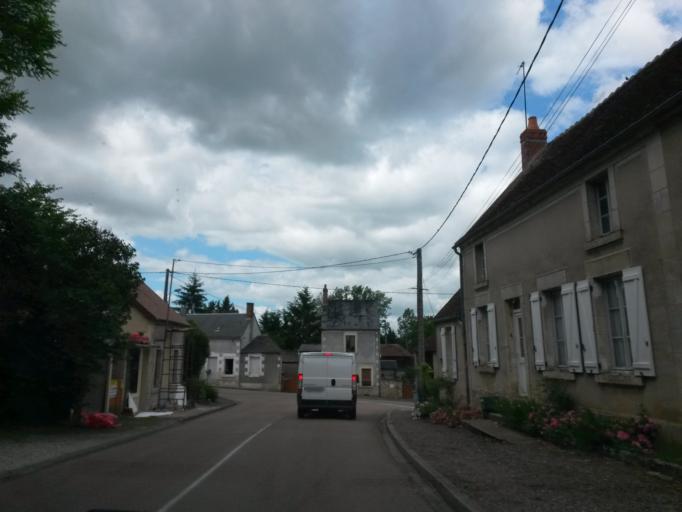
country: FR
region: Bourgogne
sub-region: Departement de la Nievre
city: La Charite-sur-Loire
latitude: 47.2355
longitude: 3.0694
